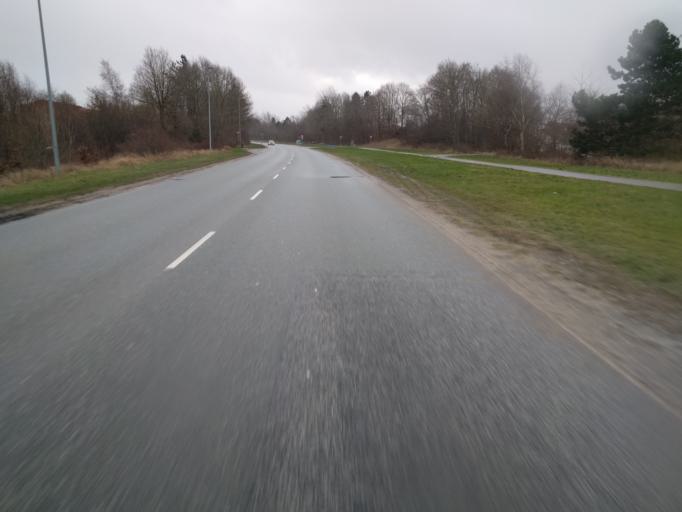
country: DK
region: Central Jutland
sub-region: Viborg Kommune
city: Viborg
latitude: 56.4588
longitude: 9.4447
